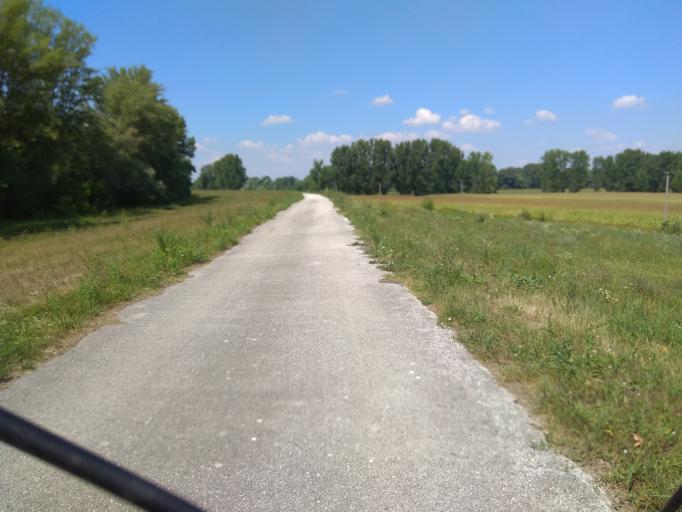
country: SK
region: Trnavsky
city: Gabcikovo
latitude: 47.8143
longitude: 17.6282
